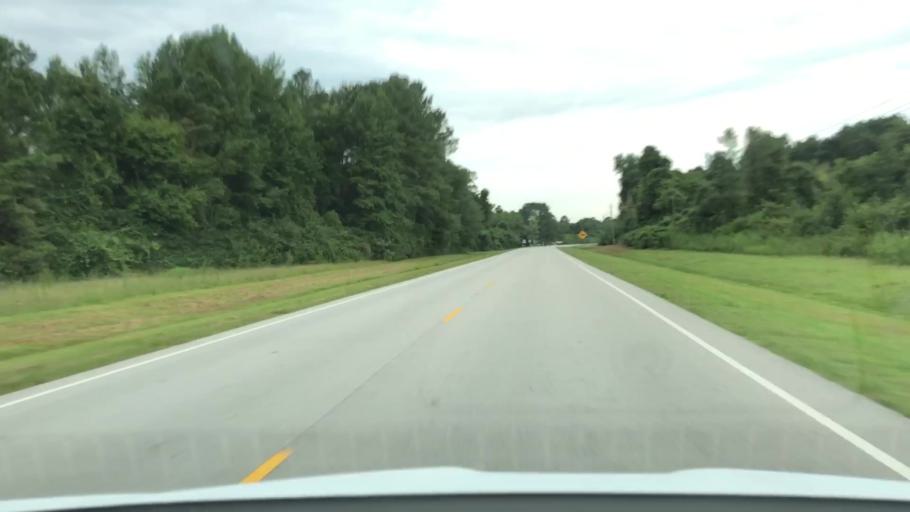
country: US
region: North Carolina
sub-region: Jones County
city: Trenton
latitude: 35.0169
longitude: -77.2986
